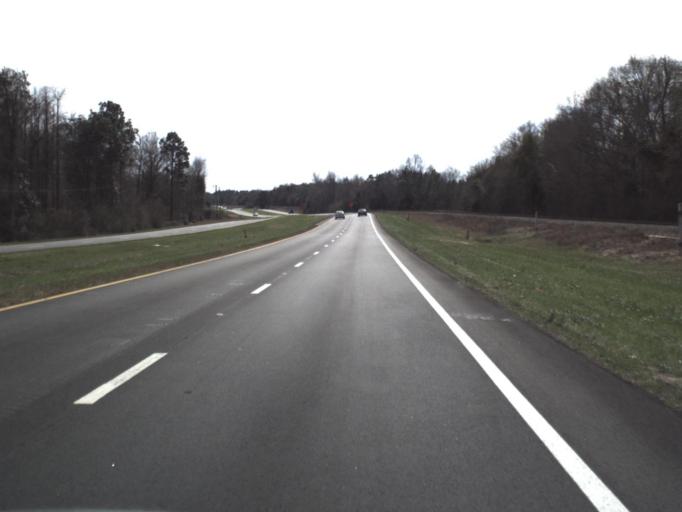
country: US
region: Florida
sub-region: Washington County
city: Chipley
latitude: 30.6774
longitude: -85.3941
